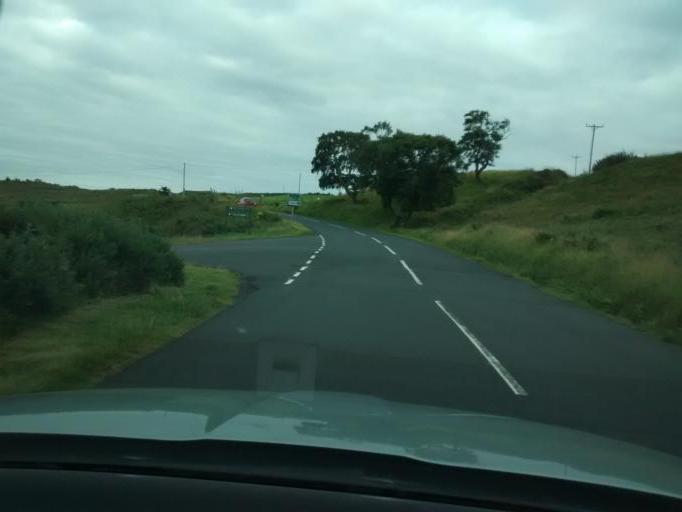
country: GB
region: Scotland
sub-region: North Ayrshire
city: Isle of Arran
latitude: 55.6694
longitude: -5.1685
